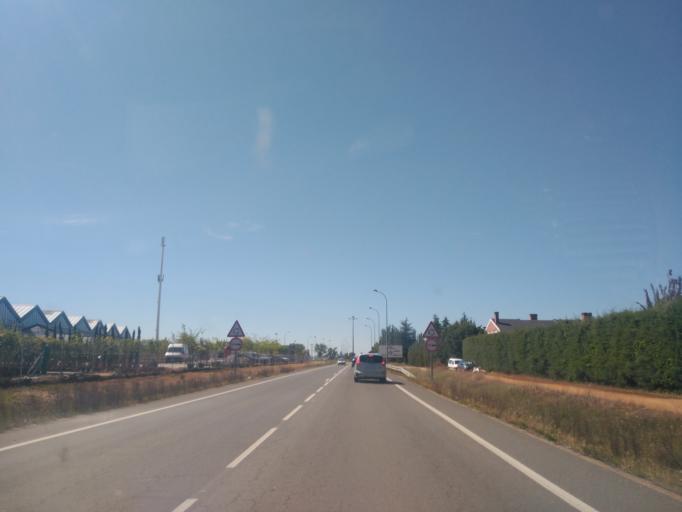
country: ES
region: Castille and Leon
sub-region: Provincia de Salamanca
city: Santa Marta de Tormes
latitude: 40.9323
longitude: -5.6249
